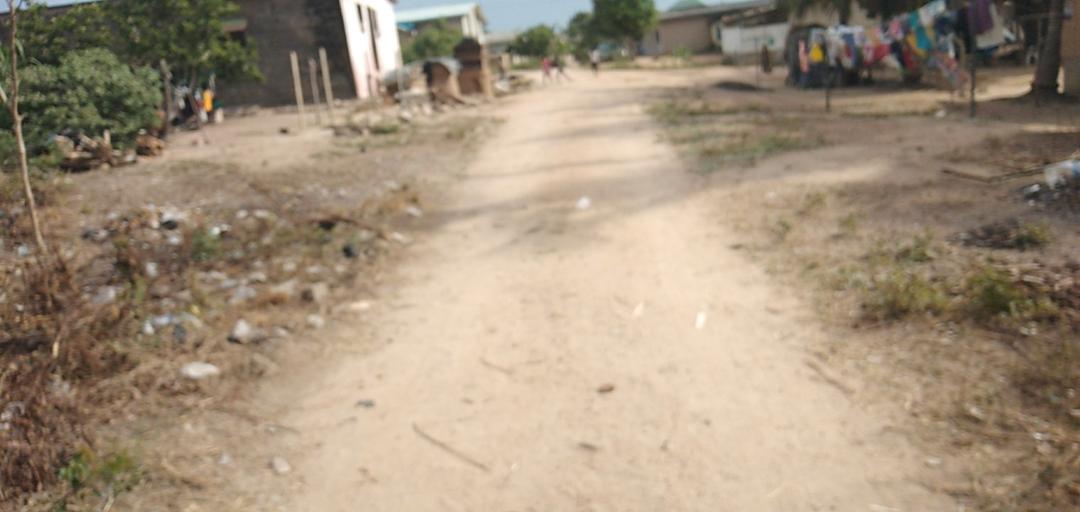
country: GH
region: Central
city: Winneba
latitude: 5.3581
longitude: -0.6188
